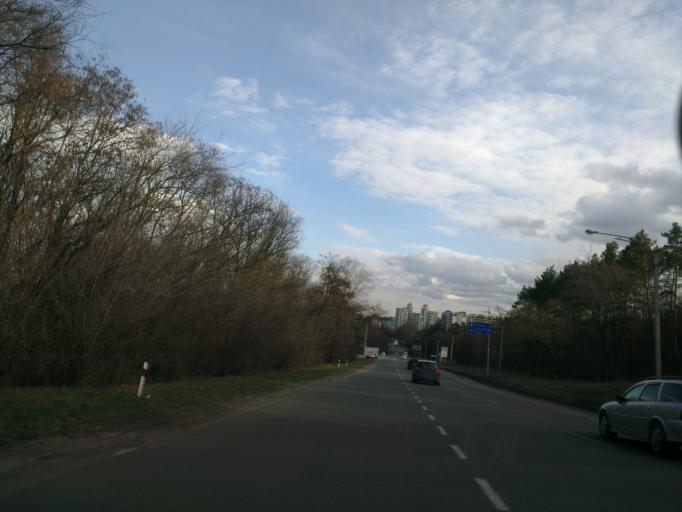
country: MD
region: Chisinau
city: Vatra
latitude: 47.0517
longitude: 28.7733
